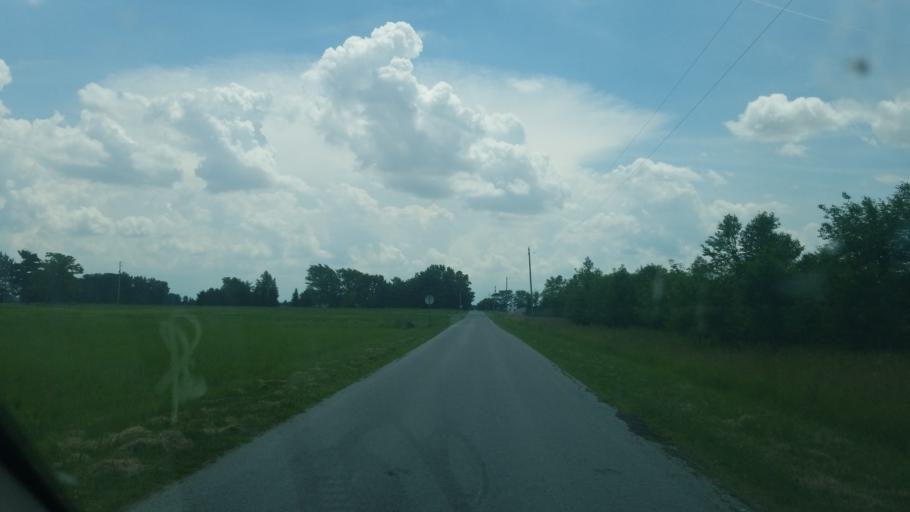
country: US
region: Ohio
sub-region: Hardin County
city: Forest
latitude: 40.7913
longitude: -83.6050
